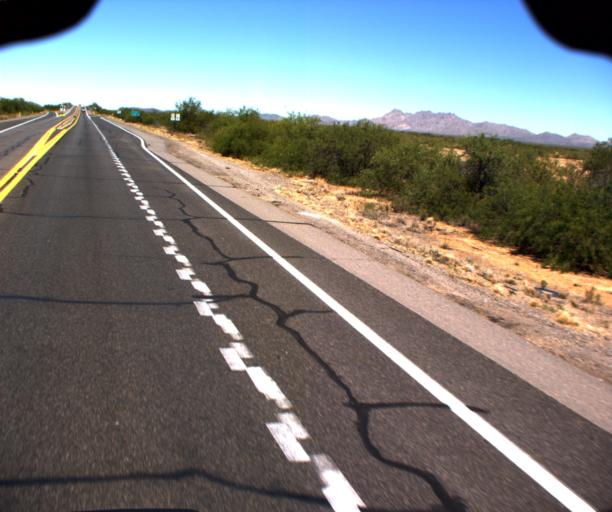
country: US
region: Arizona
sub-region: Yavapai County
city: Congress
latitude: 34.1195
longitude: -112.9448
